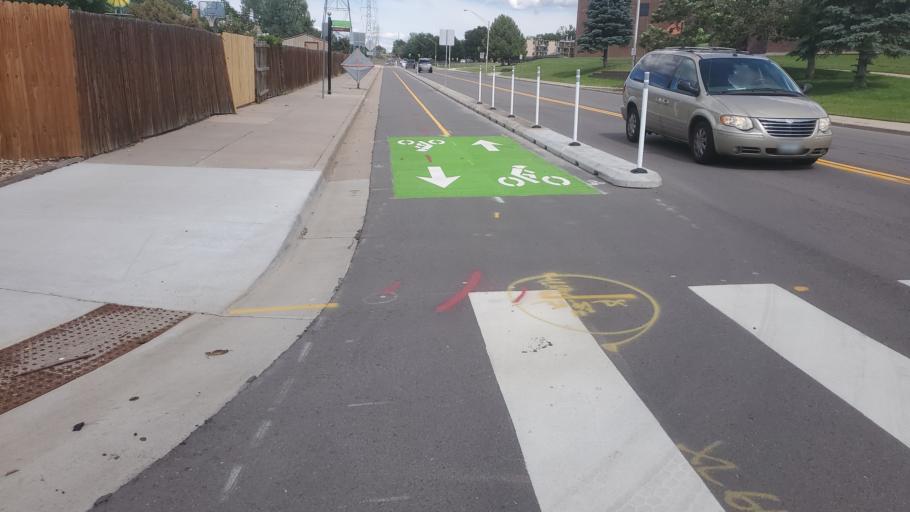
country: US
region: Colorado
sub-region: Adams County
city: Aurora
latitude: 39.6821
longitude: -104.8412
